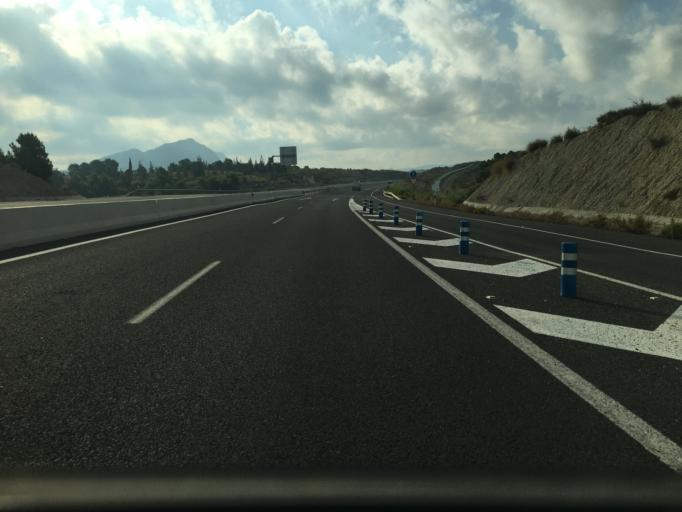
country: ES
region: Murcia
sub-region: Murcia
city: Beniel
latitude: 37.9963
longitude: -0.9823
